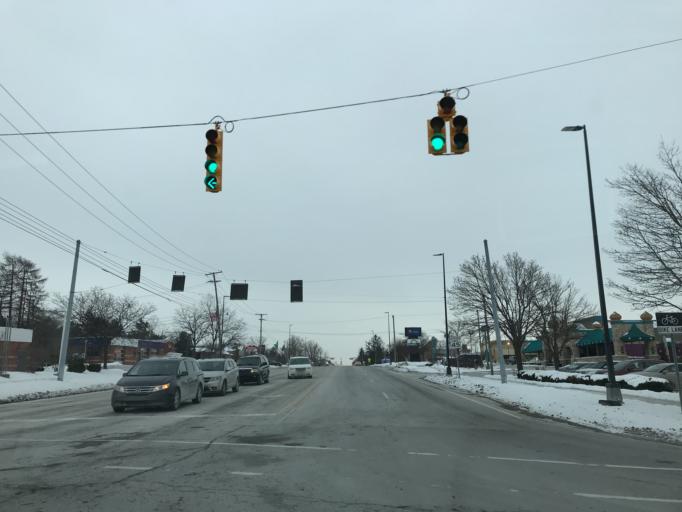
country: US
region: Michigan
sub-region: Washtenaw County
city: Ann Arbor
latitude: 42.2541
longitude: -83.6808
